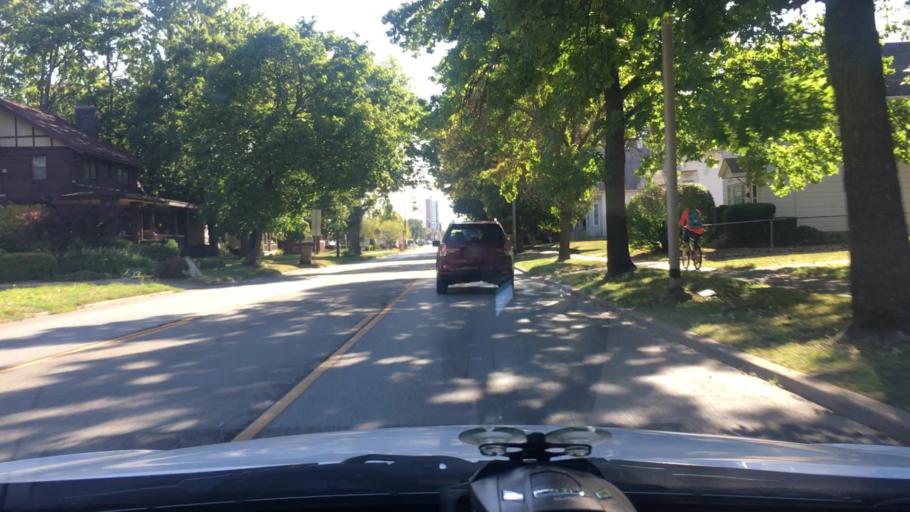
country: US
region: Illinois
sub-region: Champaign County
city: Champaign
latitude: 40.1126
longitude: -88.2498
